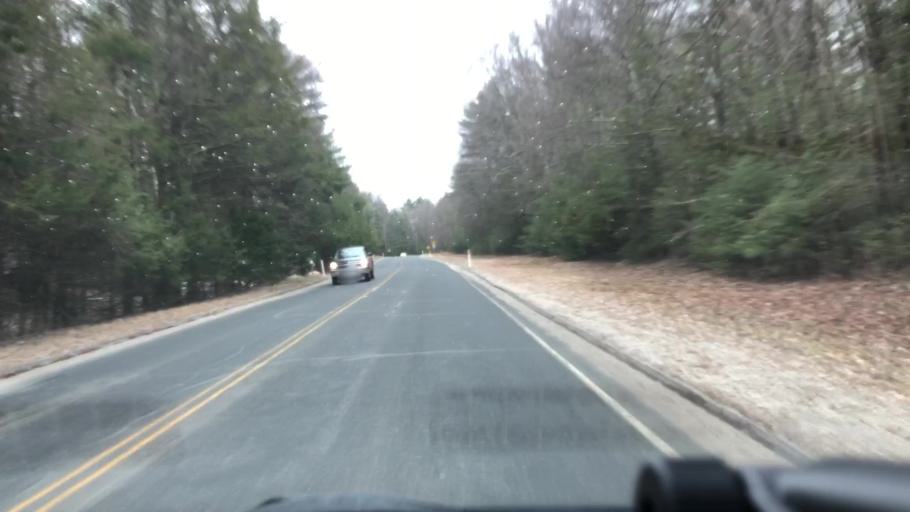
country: US
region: Massachusetts
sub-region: Hampshire County
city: Southampton
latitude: 42.2634
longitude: -72.7391
